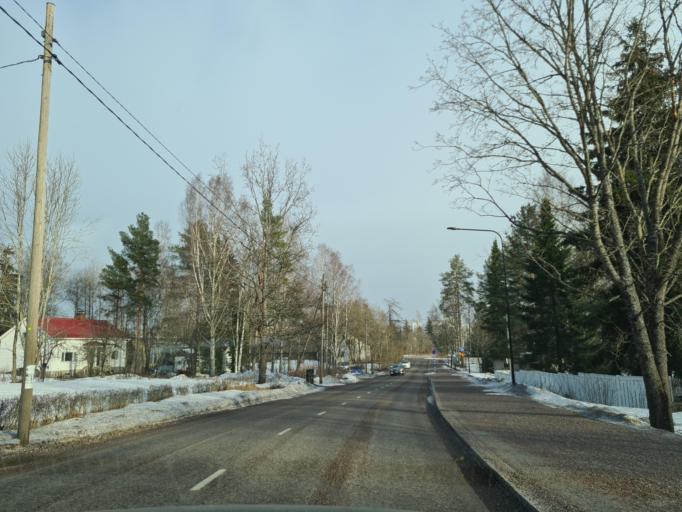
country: FI
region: Uusimaa
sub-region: Helsinki
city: Maentsaelae
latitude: 60.6392
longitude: 25.3144
